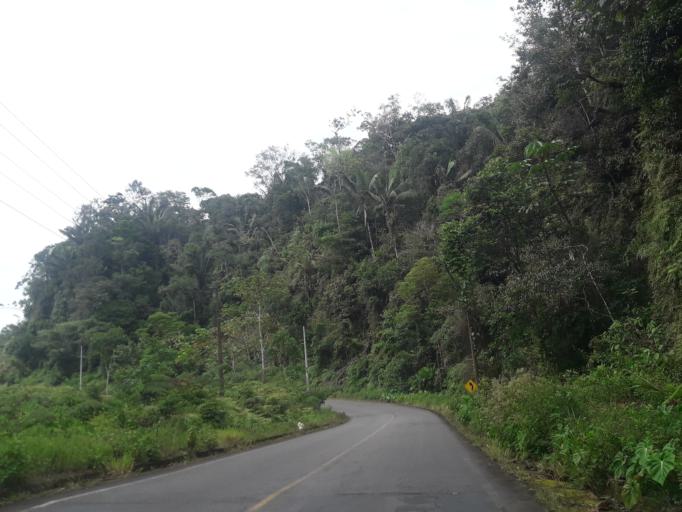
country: EC
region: Napo
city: Tena
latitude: -1.0505
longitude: -77.8969
